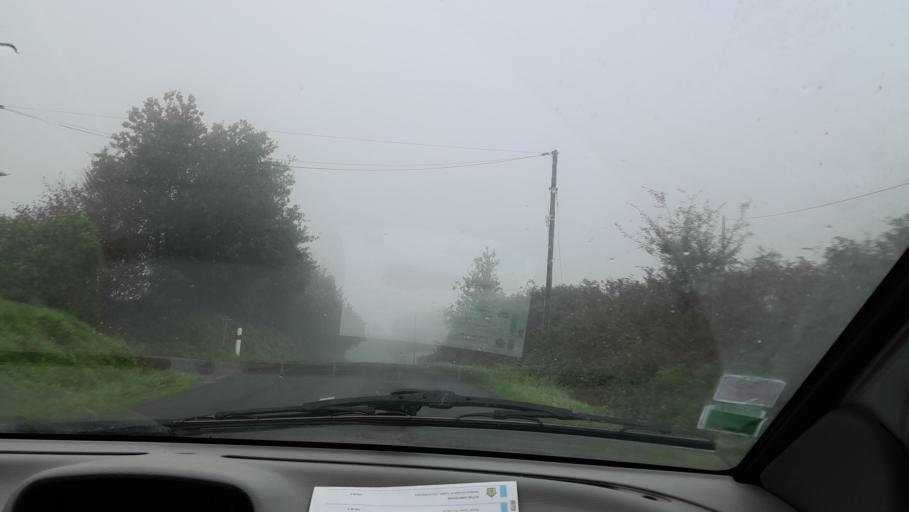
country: FR
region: Pays de la Loire
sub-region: Departement de la Mayenne
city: Saint-Pierre-la-Cour
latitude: 48.0848
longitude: -1.0175
